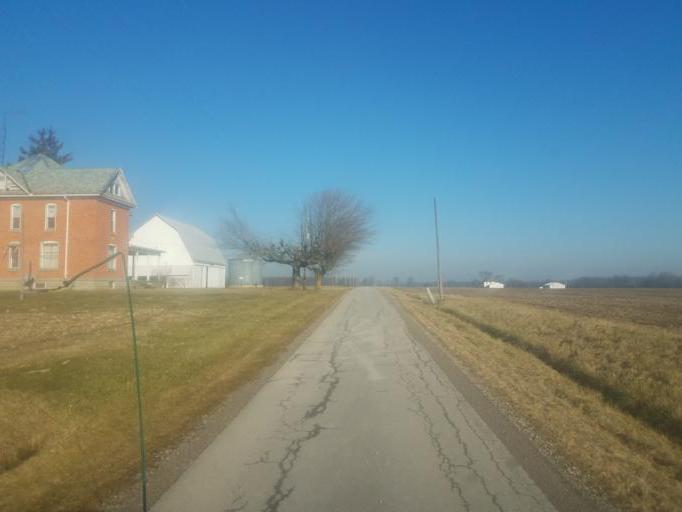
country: US
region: Ohio
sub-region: Huron County
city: Willard
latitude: 41.0319
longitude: -82.9391
